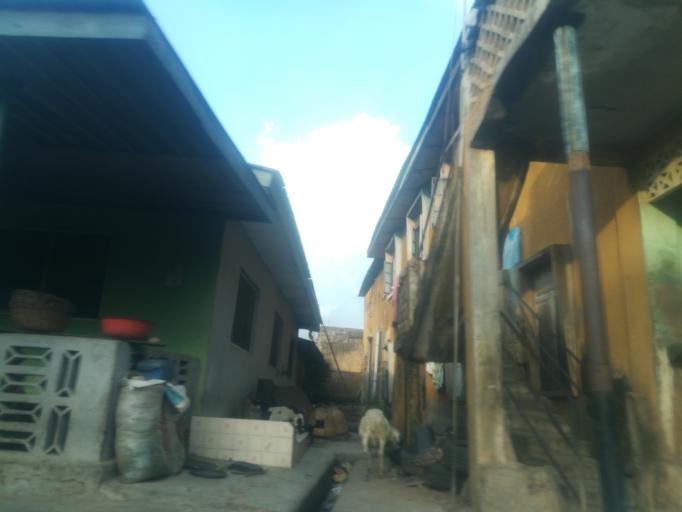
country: NG
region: Oyo
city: Ibadan
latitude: 7.3790
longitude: 3.8542
